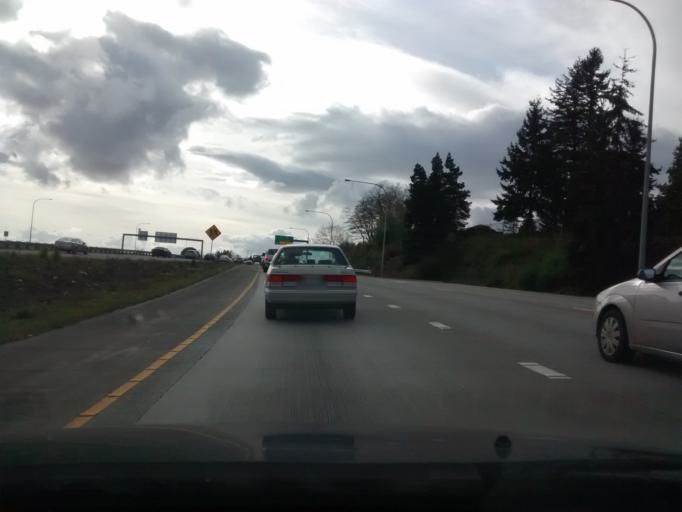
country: US
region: Washington
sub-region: Pierce County
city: Tacoma
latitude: 47.2354
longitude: -122.4680
